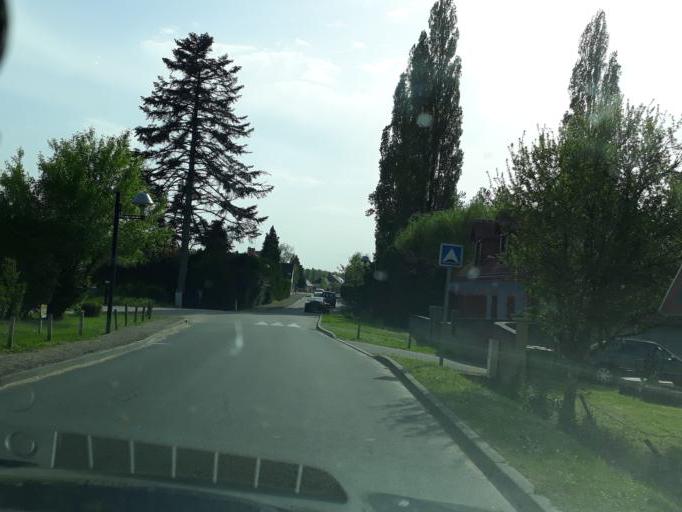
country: FR
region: Centre
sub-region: Departement du Loir-et-Cher
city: Saint-Laurent-Nouan
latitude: 47.6526
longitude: 1.6120
